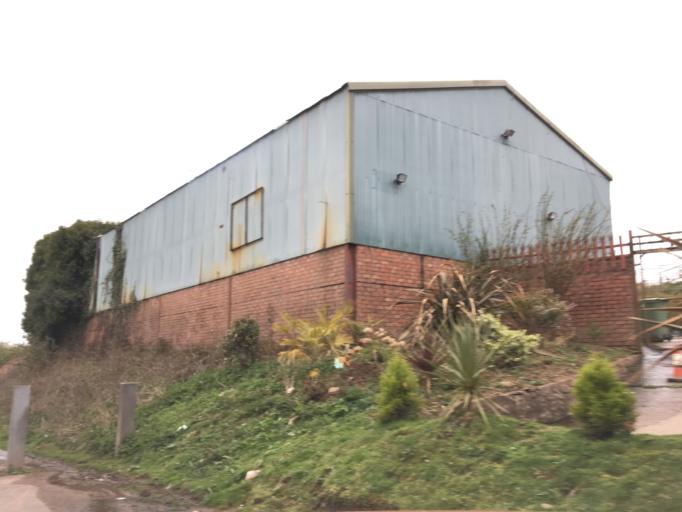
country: GB
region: Wales
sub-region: Newport
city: Marshfield
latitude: 51.5308
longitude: -3.1260
